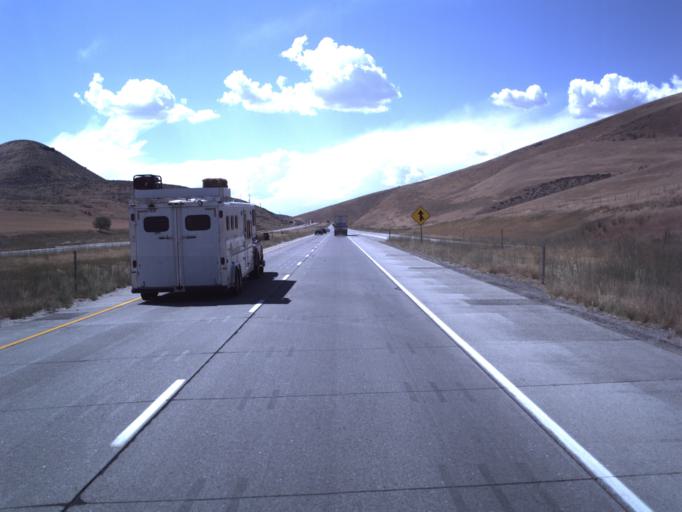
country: US
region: Utah
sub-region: Box Elder County
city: Garland
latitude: 41.8007
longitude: -112.3067
